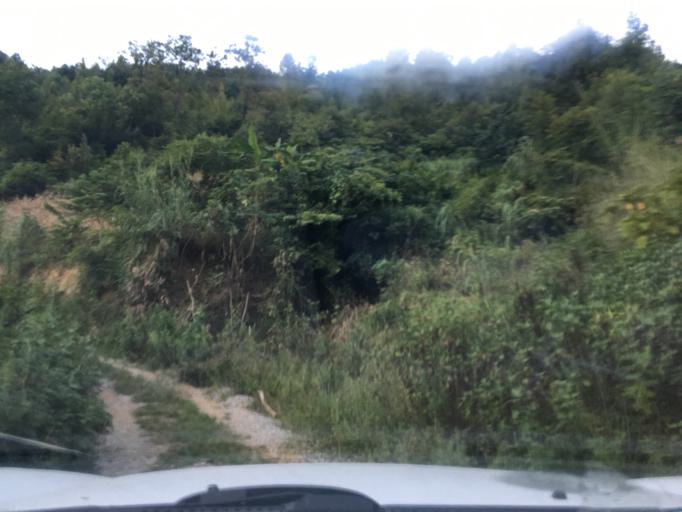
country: CN
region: Guangxi Zhuangzu Zizhiqu
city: Xinzhou
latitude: 25.3513
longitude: 105.7418
